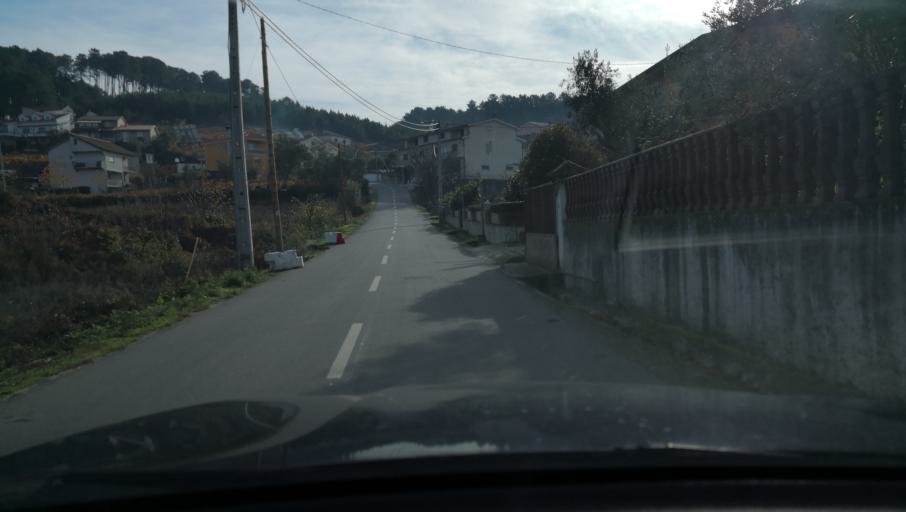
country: PT
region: Vila Real
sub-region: Vila Real
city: Vila Real
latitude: 41.2866
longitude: -7.7098
